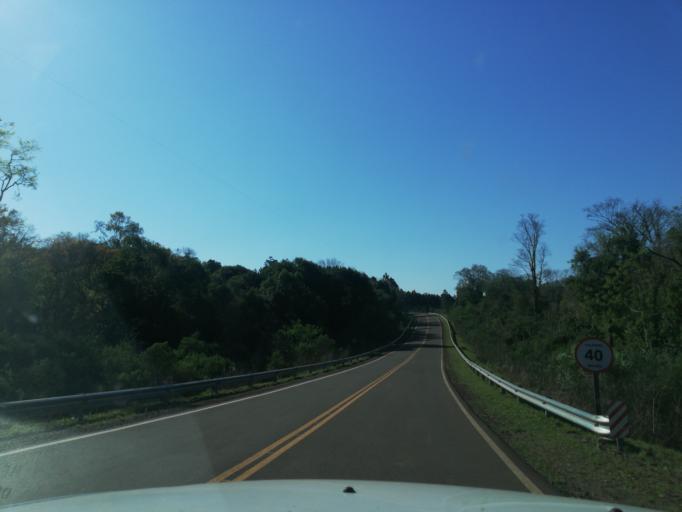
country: AR
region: Misiones
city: Arroyo del Medio
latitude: -27.6817
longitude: -55.3988
